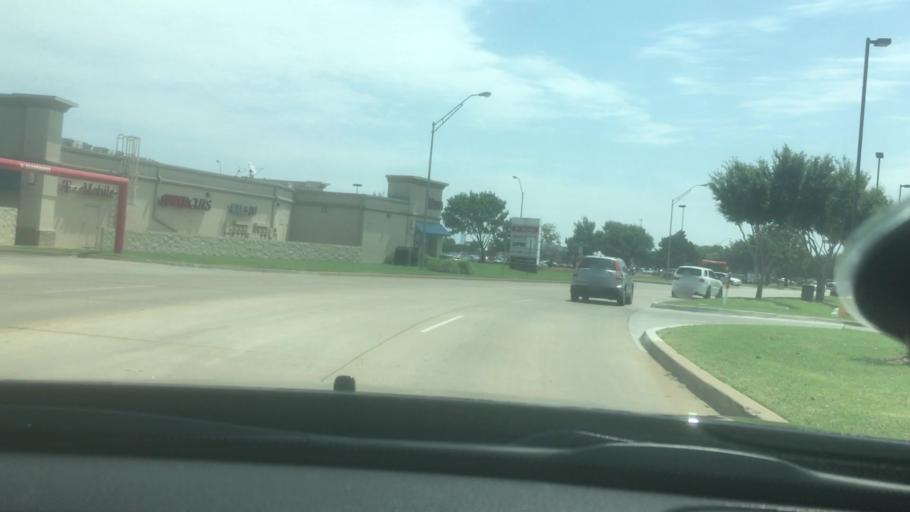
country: US
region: Oklahoma
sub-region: Oklahoma County
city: Bethany
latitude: 35.4619
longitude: -97.6257
